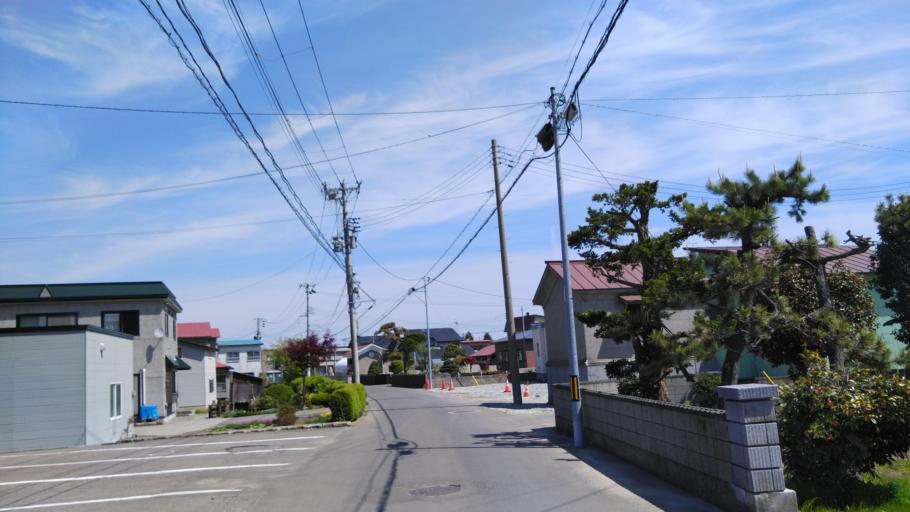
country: JP
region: Aomori
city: Aomori Shi
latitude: 40.8301
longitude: 140.6982
